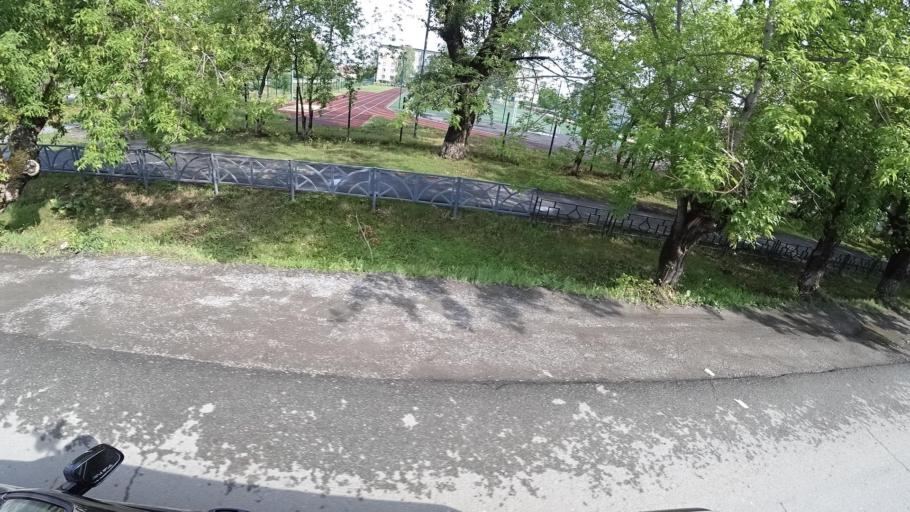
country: RU
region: Sverdlovsk
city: Kamyshlov
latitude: 56.8422
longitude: 62.7152
